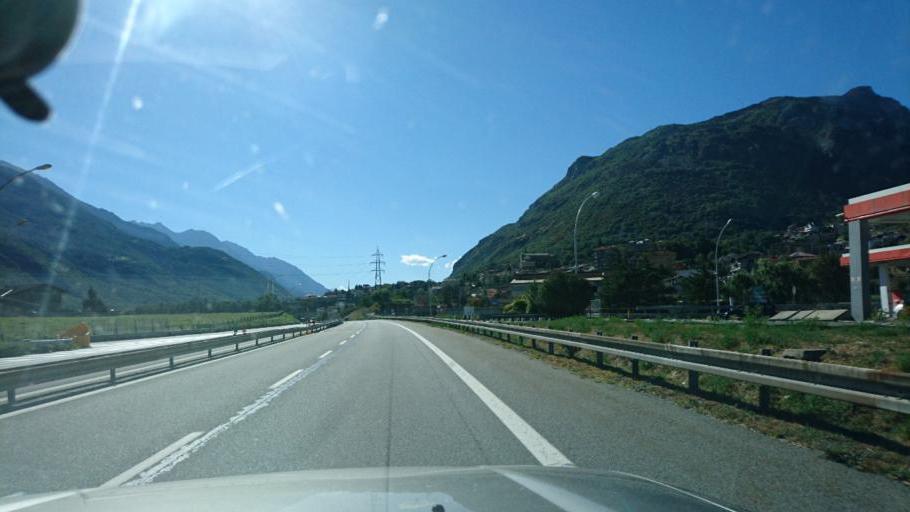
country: IT
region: Aosta Valley
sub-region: Valle d'Aosta
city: Chatillon
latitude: 45.7479
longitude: 7.6226
